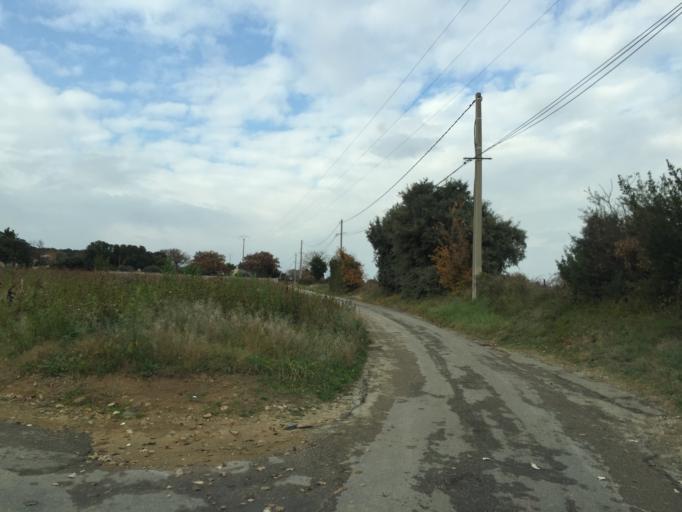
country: FR
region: Provence-Alpes-Cote d'Azur
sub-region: Departement du Vaucluse
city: Bedarrides
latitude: 44.0448
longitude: 4.8844
